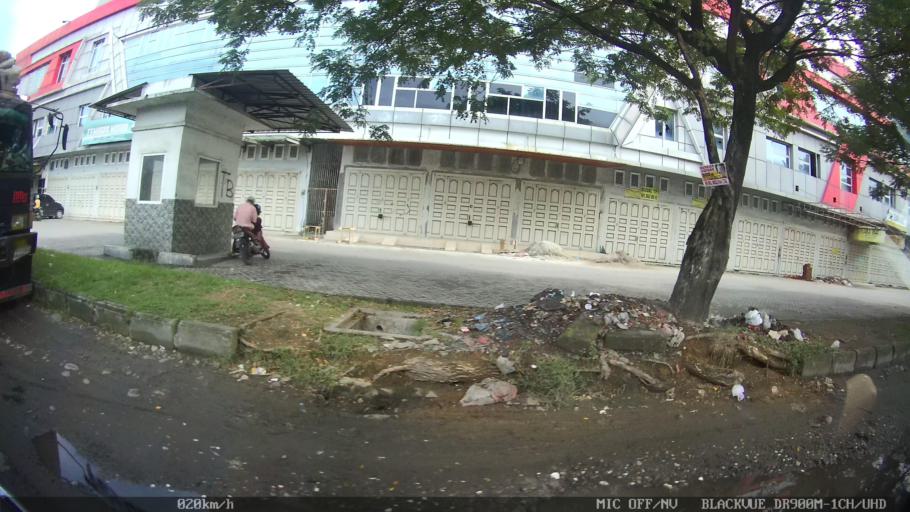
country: ID
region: North Sumatra
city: Medan
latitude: 3.6317
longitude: 98.6976
